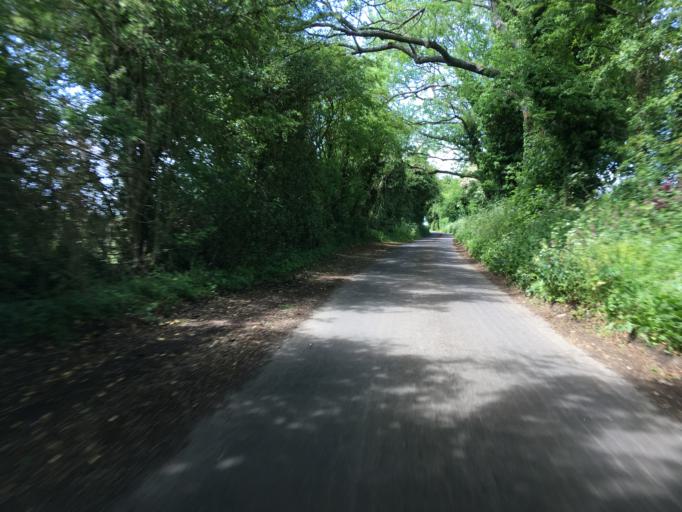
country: GB
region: England
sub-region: Gloucestershire
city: Painswick
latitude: 51.7849
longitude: -2.1372
